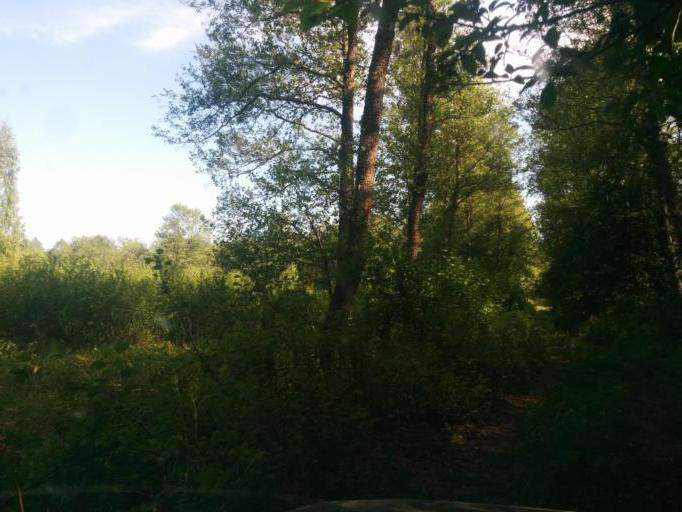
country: LV
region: Dundaga
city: Dundaga
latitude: 57.6275
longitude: 22.1131
